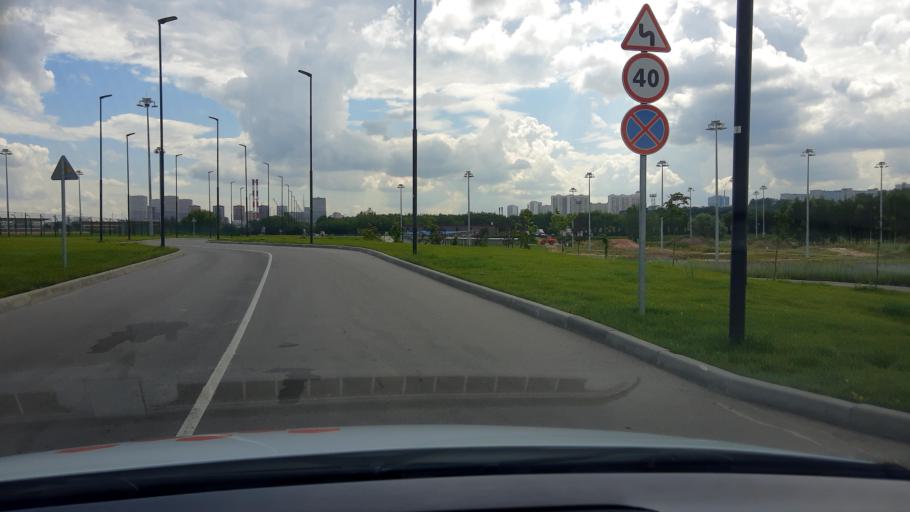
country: RU
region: Moscow
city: Kolomenskoye
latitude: 55.6537
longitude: 37.6774
